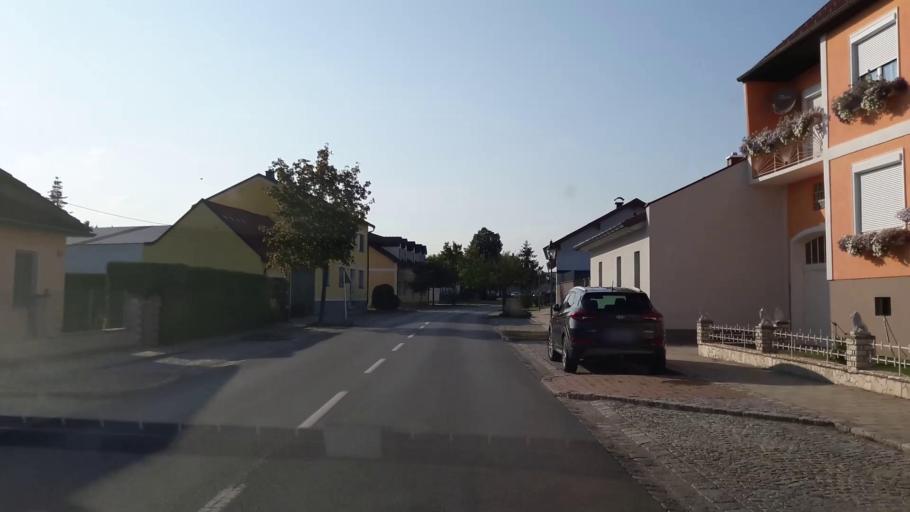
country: AT
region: Lower Austria
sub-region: Politischer Bezirk Bruck an der Leitha
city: Bruck an der Leitha
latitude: 48.0465
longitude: 16.7404
